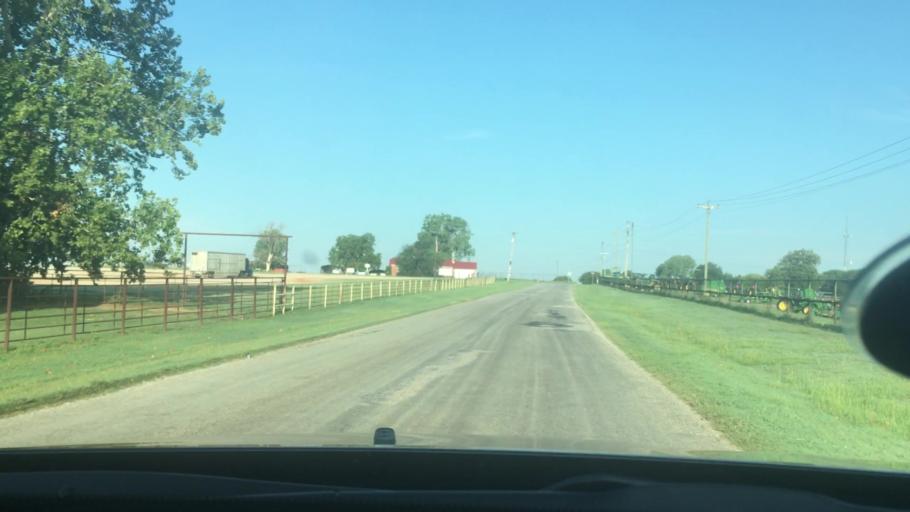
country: US
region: Oklahoma
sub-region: Pontotoc County
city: Ada
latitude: 34.7818
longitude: -96.7200
